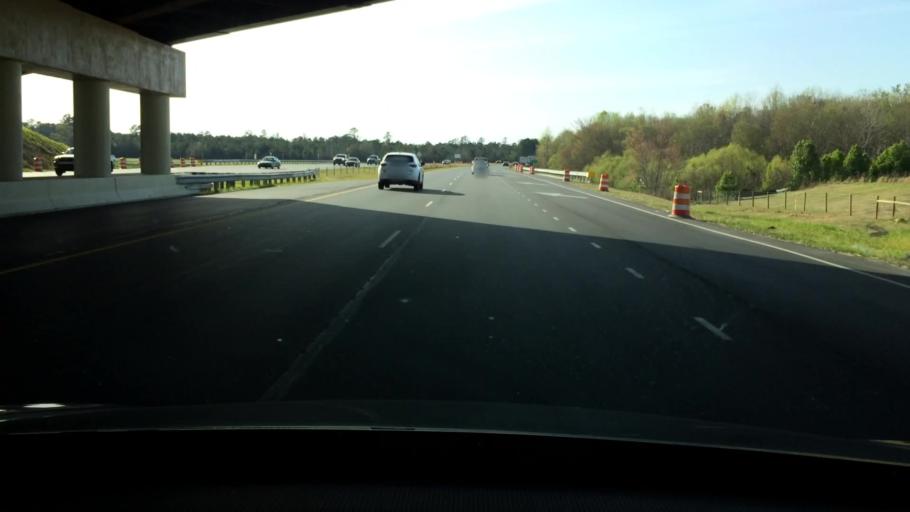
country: US
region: North Carolina
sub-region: Johnston County
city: Pine Level
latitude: 35.4914
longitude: -78.2698
